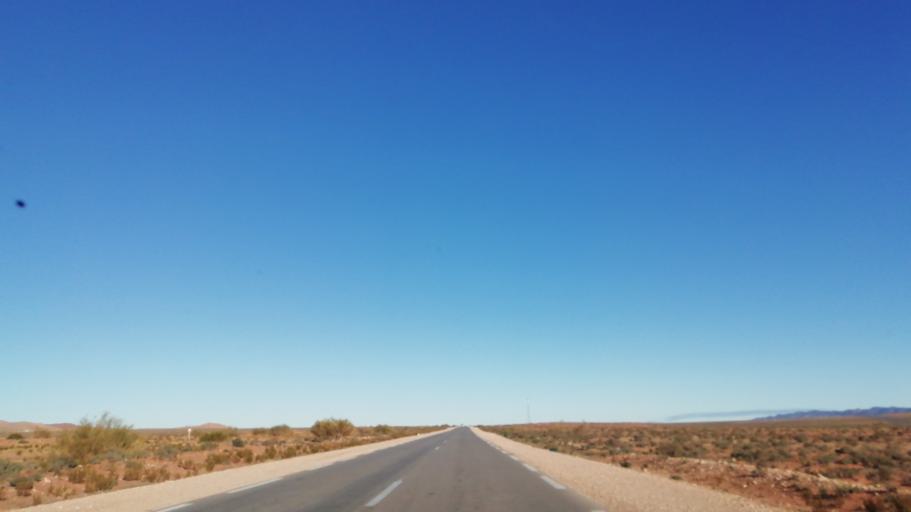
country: DZ
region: El Bayadh
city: El Abiodh Sidi Cheikh
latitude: 33.1121
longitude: 0.2287
